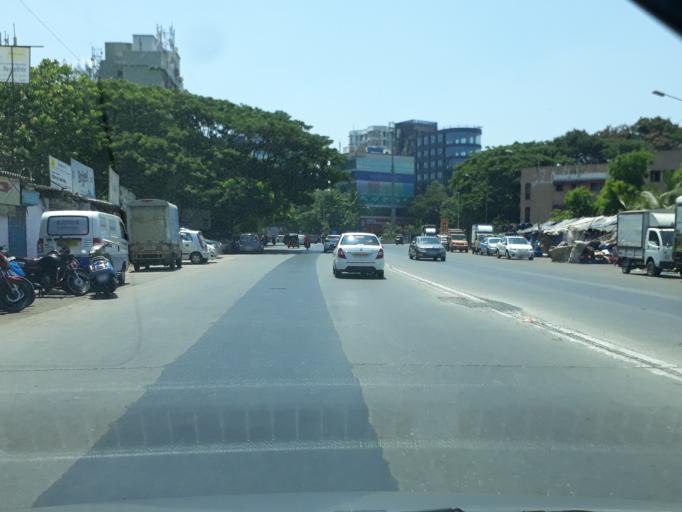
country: IN
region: Maharashtra
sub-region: Mumbai Suburban
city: Mumbai
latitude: 19.0748
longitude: 72.8588
